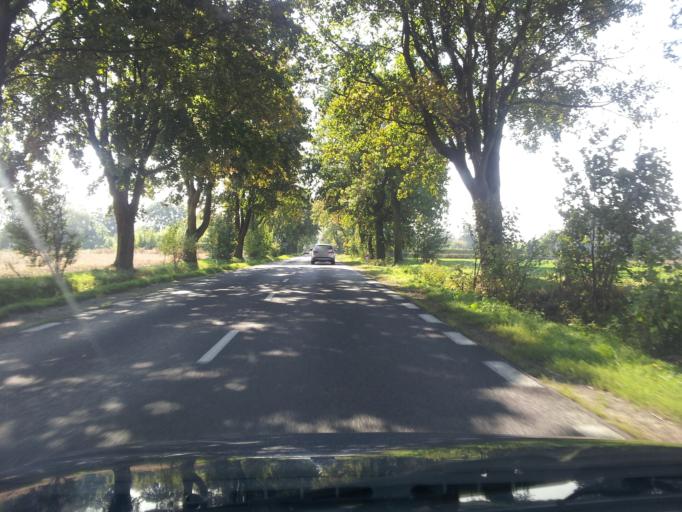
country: PL
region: Masovian Voivodeship
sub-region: Powiat sierpecki
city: Sierpc
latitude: 52.8702
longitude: 19.6618
